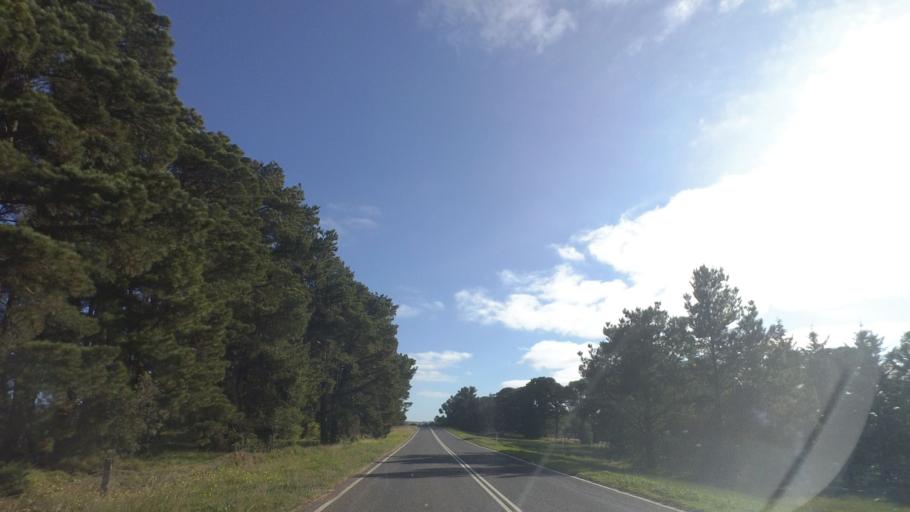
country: AU
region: Victoria
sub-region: Hume
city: Sunbury
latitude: -37.5365
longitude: 144.6731
